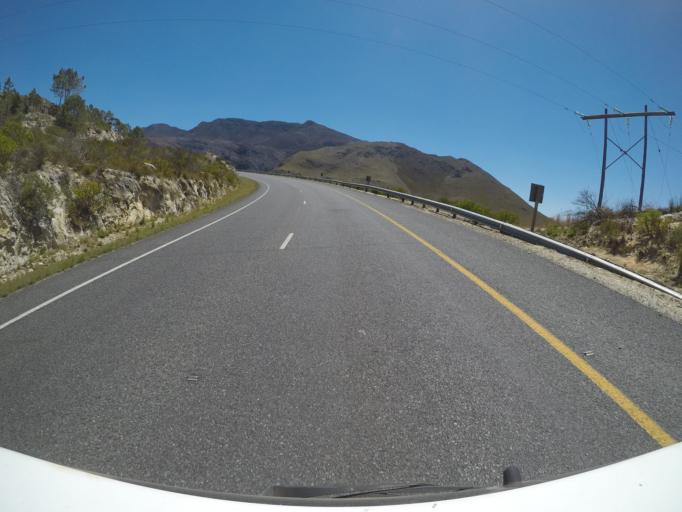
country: ZA
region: Western Cape
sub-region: Overberg District Municipality
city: Grabouw
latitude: -34.2195
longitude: 19.1897
